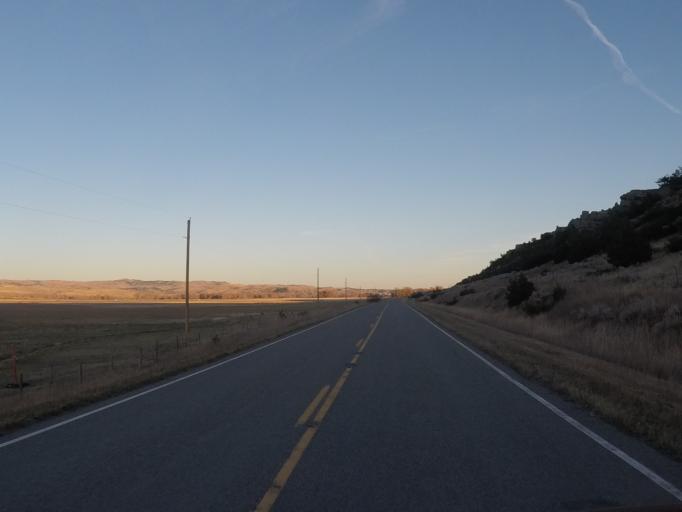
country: US
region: Montana
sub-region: Sweet Grass County
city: Big Timber
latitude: 45.7813
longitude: -109.8235
